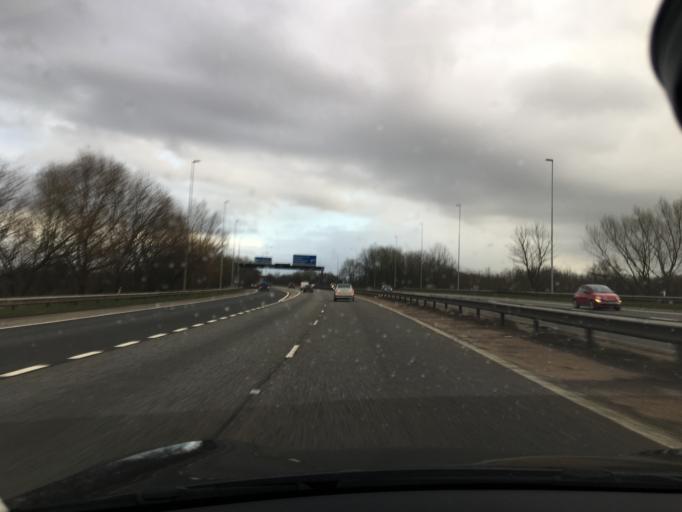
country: GB
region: England
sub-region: Manchester
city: Didsbury
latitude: 53.4007
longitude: -2.2421
